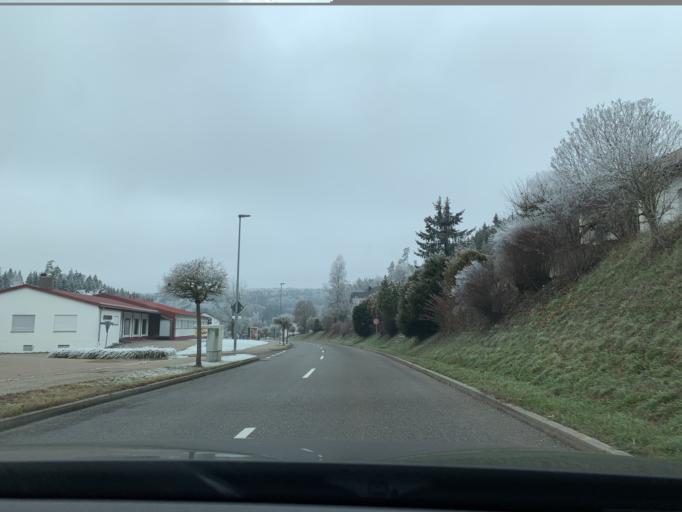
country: DE
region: Baden-Wuerttemberg
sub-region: Freiburg Region
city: Tengen
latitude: 47.8684
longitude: 8.6610
